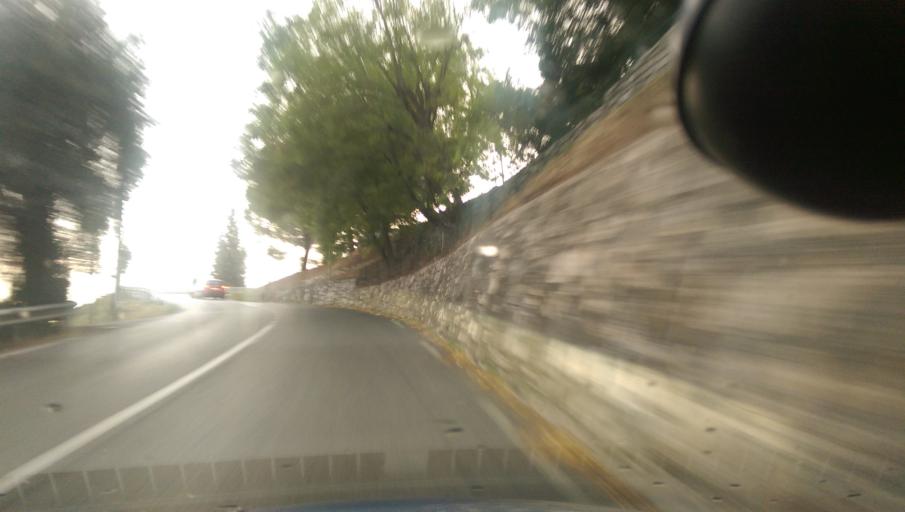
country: FR
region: Provence-Alpes-Cote d'Azur
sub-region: Departement des Alpes-Maritimes
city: Opio
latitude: 43.6751
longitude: 6.9778
